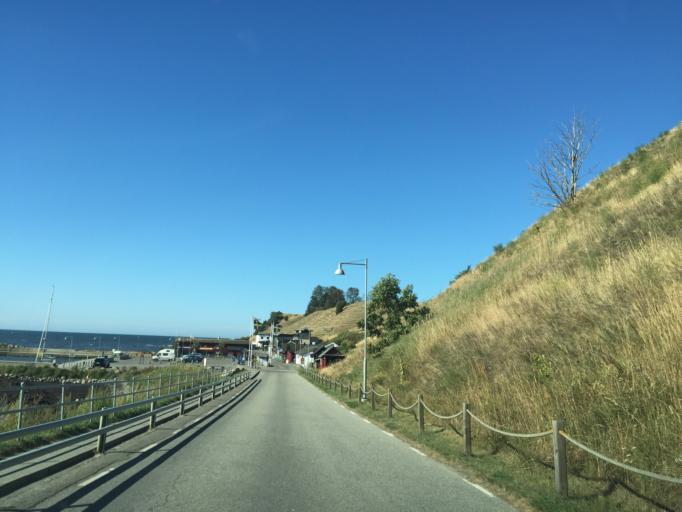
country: SE
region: Skane
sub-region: Ystads Kommun
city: Kopingebro
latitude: 55.3844
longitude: 14.0647
